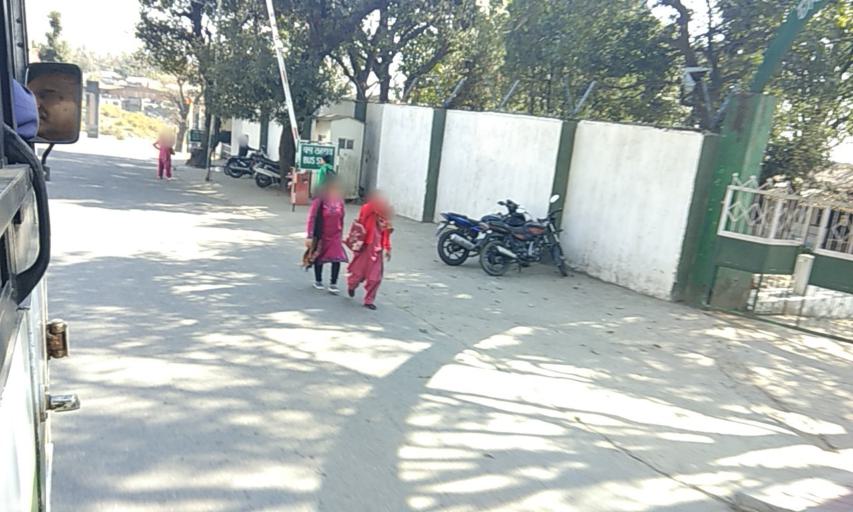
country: IN
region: Himachal Pradesh
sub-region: Kangra
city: Dharmsala
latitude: 32.1735
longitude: 76.3852
